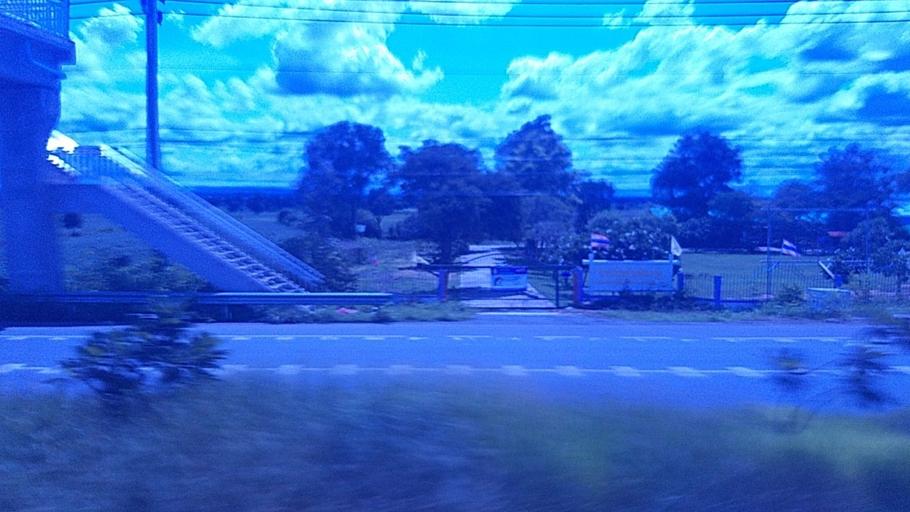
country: TH
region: Nakhon Ratchasima
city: Dan Khun Thot
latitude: 15.0952
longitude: 101.7206
